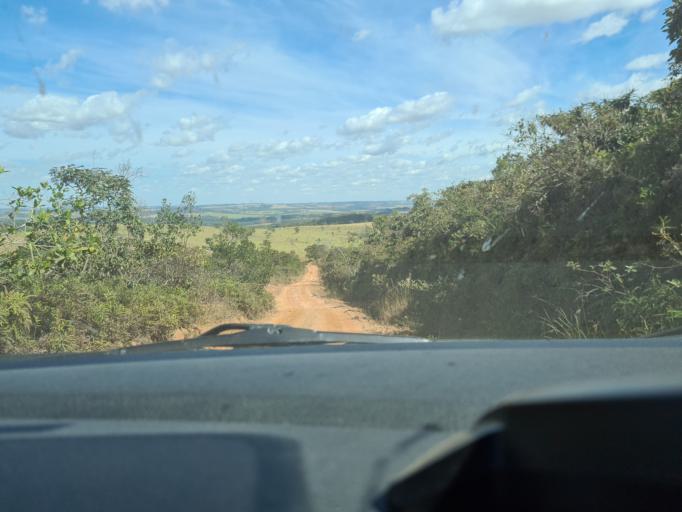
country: BR
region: Goias
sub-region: Silvania
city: Silvania
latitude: -16.5323
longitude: -48.5525
